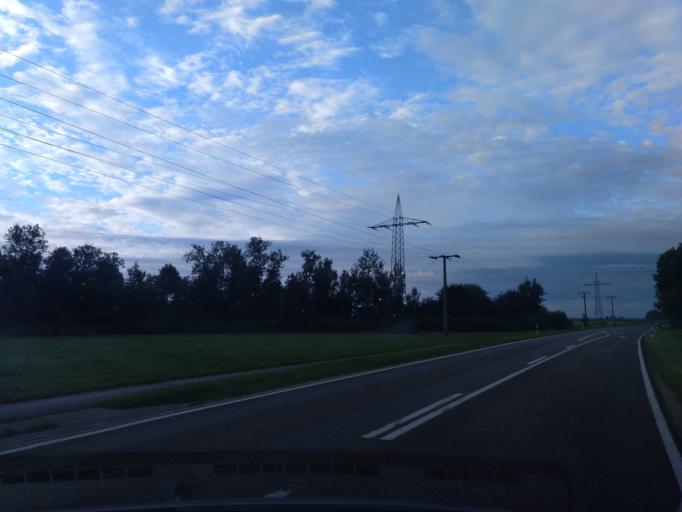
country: DE
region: Bavaria
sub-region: Upper Bavaria
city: Burgheim
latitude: 48.7249
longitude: 11.0140
